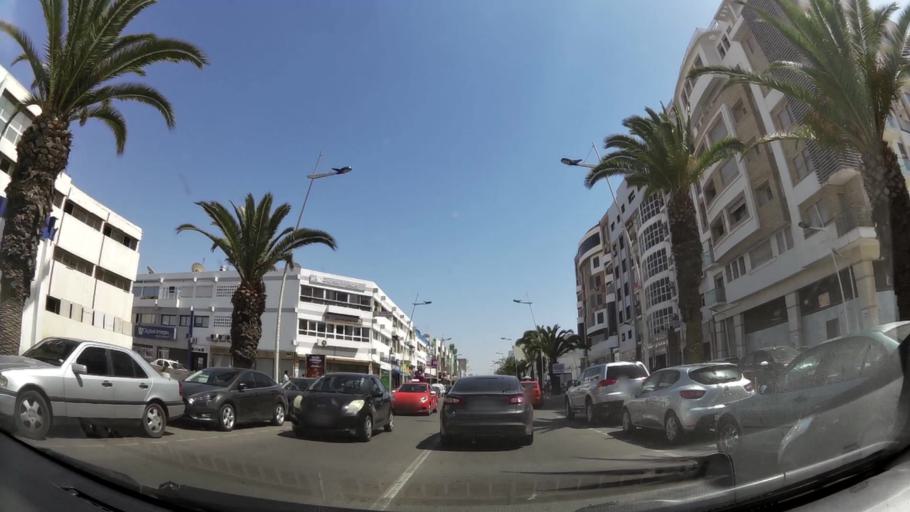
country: MA
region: Souss-Massa-Draa
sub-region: Agadir-Ida-ou-Tnan
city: Agadir
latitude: 30.4146
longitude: -9.5937
